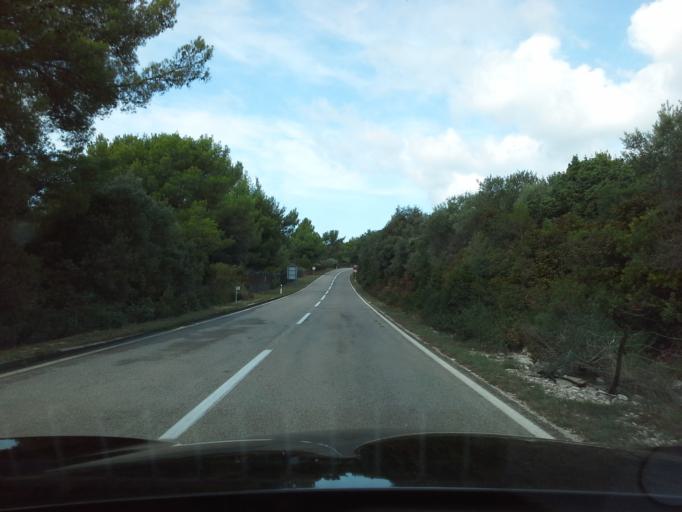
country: HR
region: Primorsko-Goranska
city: Mali Losinj
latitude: 44.5691
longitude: 14.4275
